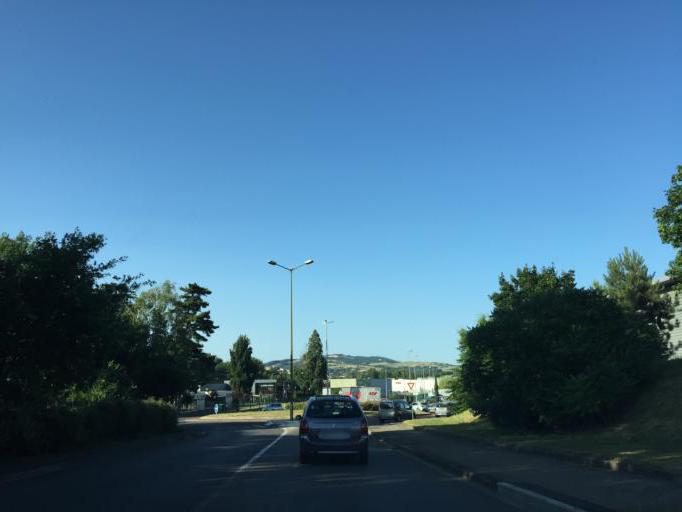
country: FR
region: Rhone-Alpes
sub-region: Departement de la Loire
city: La Talaudiere
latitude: 45.4700
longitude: 4.4352
